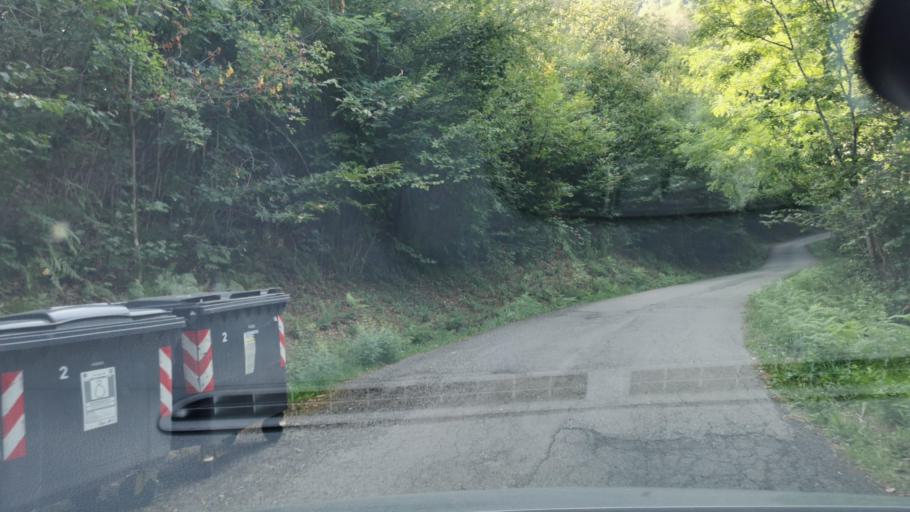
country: IT
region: Piedmont
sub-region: Provincia di Torino
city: Corio
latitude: 45.3054
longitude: 7.5220
